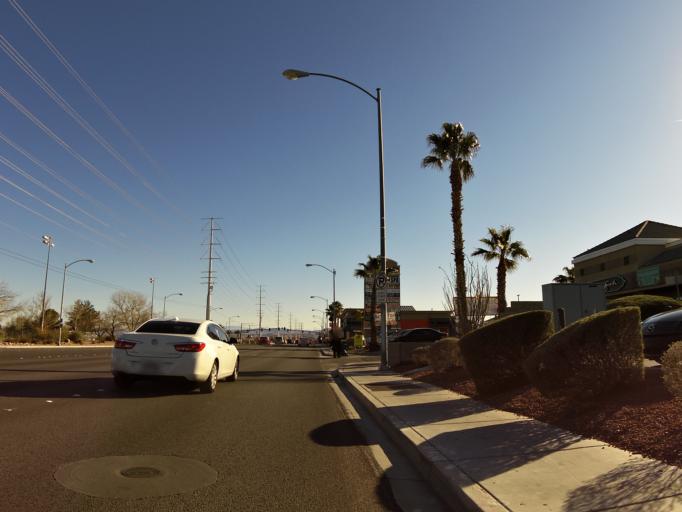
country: US
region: Nevada
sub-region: Clark County
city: Spring Valley
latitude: 36.1243
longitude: -115.2792
